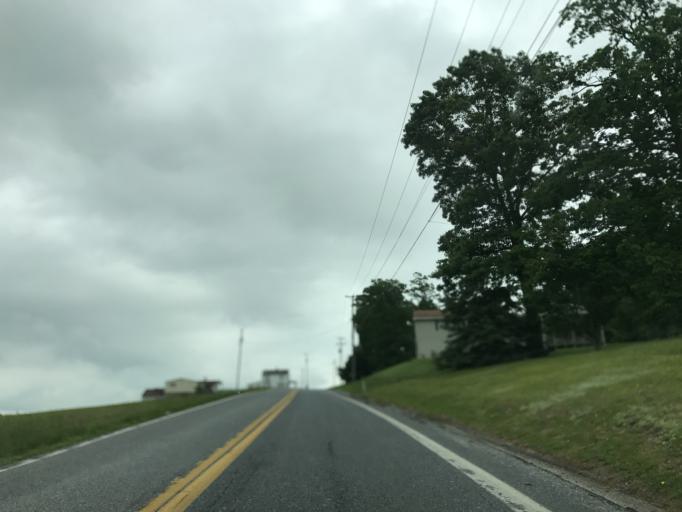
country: US
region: Pennsylvania
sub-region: York County
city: Dallastown
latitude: 39.8450
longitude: -76.6413
